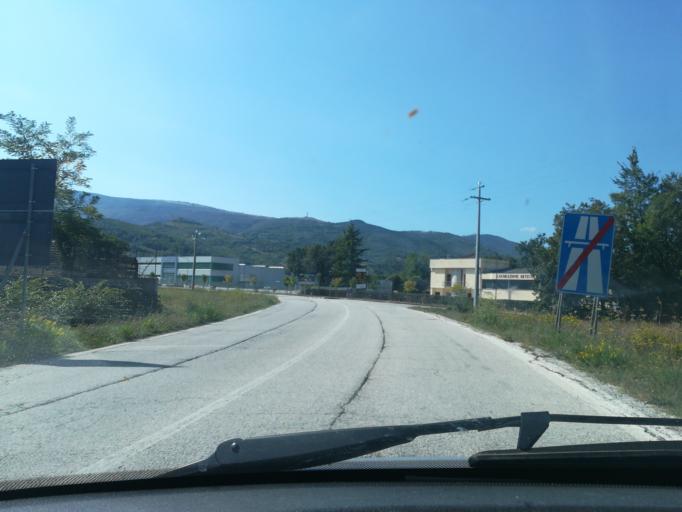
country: IT
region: The Marches
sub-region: Provincia di Macerata
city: Caldarola
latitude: 43.1485
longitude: 13.2249
